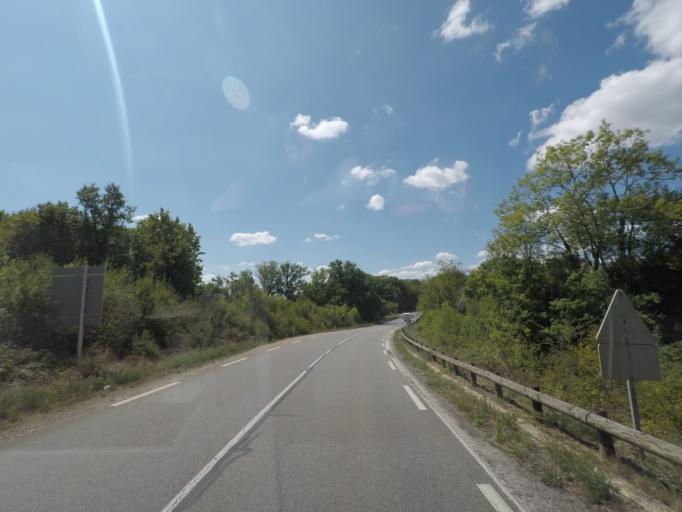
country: FR
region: Midi-Pyrenees
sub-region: Departement du Lot
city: Lacapelle-Marival
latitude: 44.6220
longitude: 1.9248
